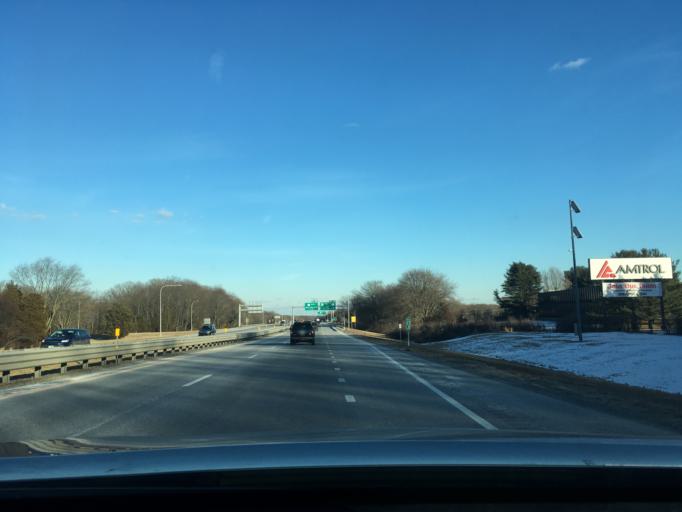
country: US
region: Rhode Island
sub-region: Kent County
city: West Warwick
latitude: 41.6664
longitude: -71.5044
